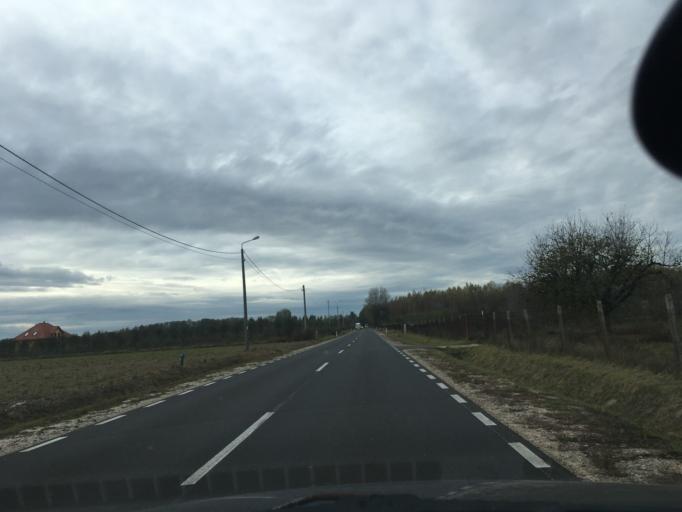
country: PL
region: Masovian Voivodeship
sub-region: Powiat grojecki
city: Pniewy
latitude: 51.9696
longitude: 20.7264
